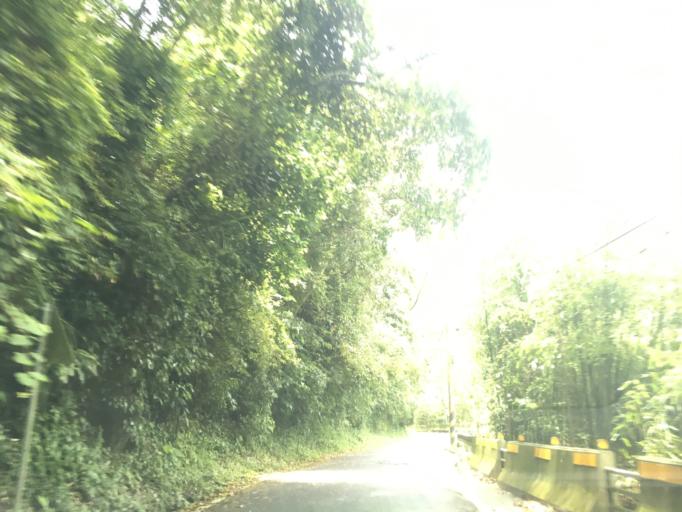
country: TW
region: Taiwan
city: Lugu
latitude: 23.5498
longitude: 120.6804
